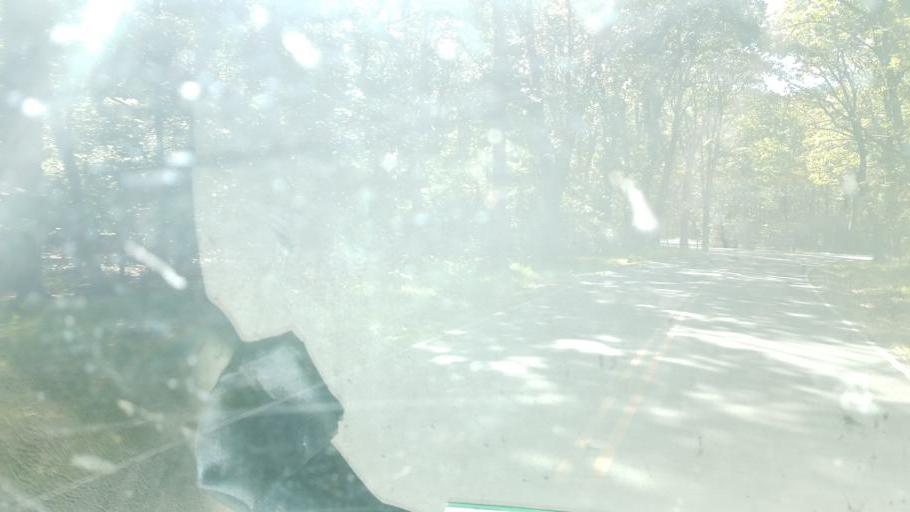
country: US
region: Virginia
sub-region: Page County
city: Stanley
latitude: 38.4405
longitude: -78.4779
